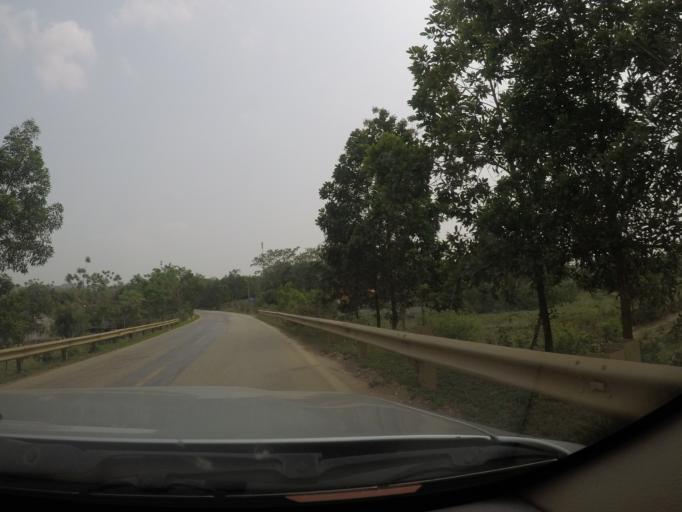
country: VN
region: Thanh Hoa
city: Thi Tran Yen Cat
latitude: 19.4829
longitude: 105.3945
